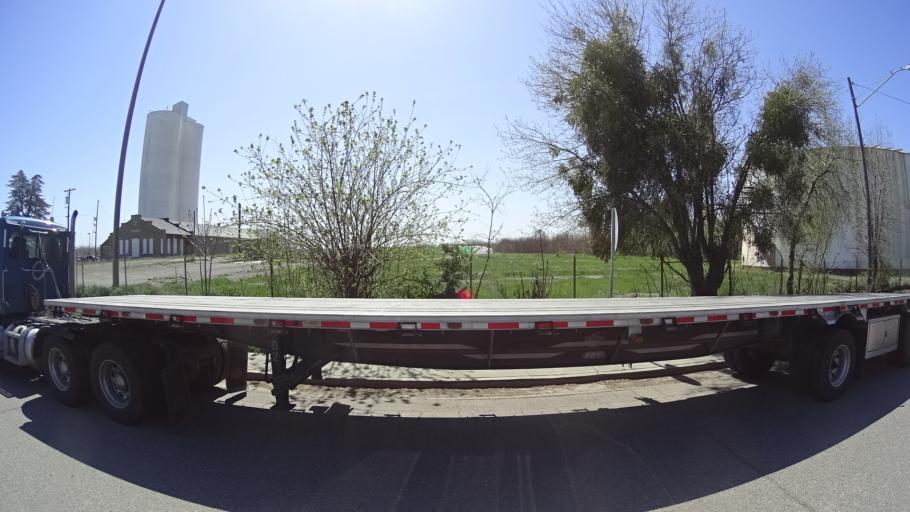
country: US
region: California
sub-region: Glenn County
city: Hamilton City
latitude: 39.7385
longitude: -122.0105
